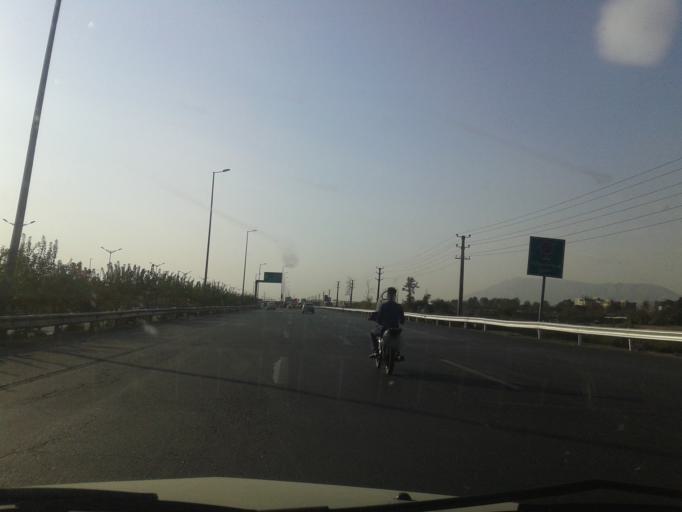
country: IR
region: Tehran
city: Eslamshahr
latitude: 35.6559
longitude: 51.2598
